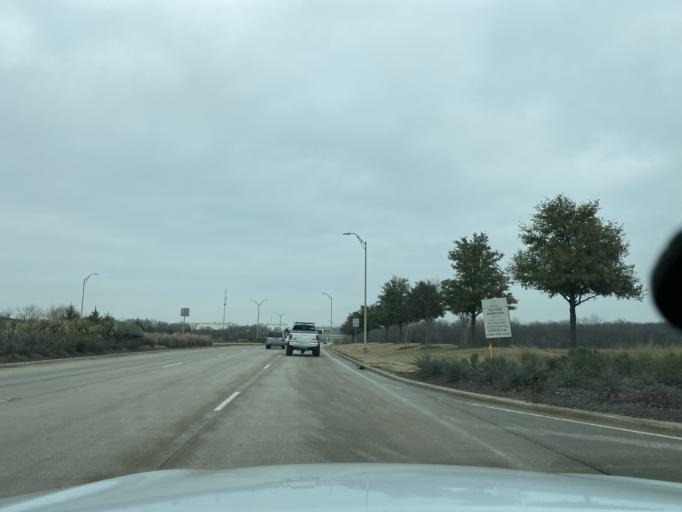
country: US
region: Texas
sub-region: Tarrant County
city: Euless
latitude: 32.8037
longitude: -97.0989
